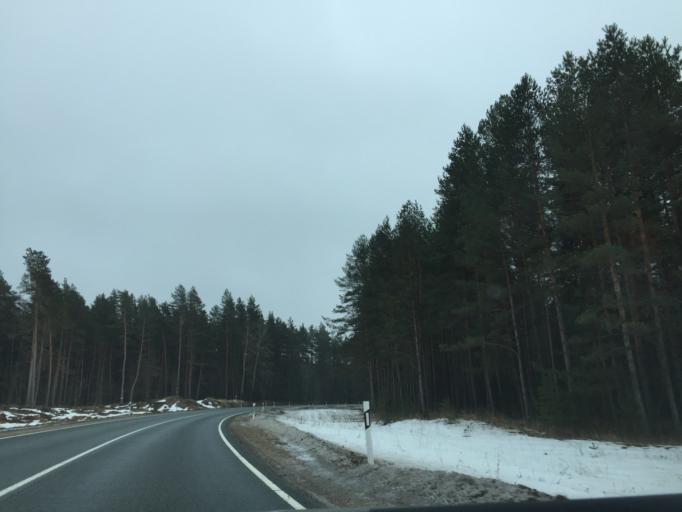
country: LV
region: Olaine
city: Olaine
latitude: 56.6232
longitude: 24.0108
